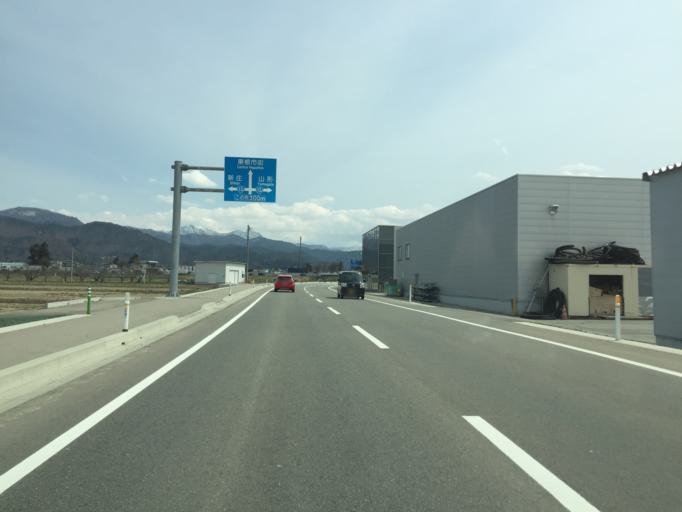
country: JP
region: Yamagata
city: Higashine
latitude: 38.4483
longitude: 140.3777
